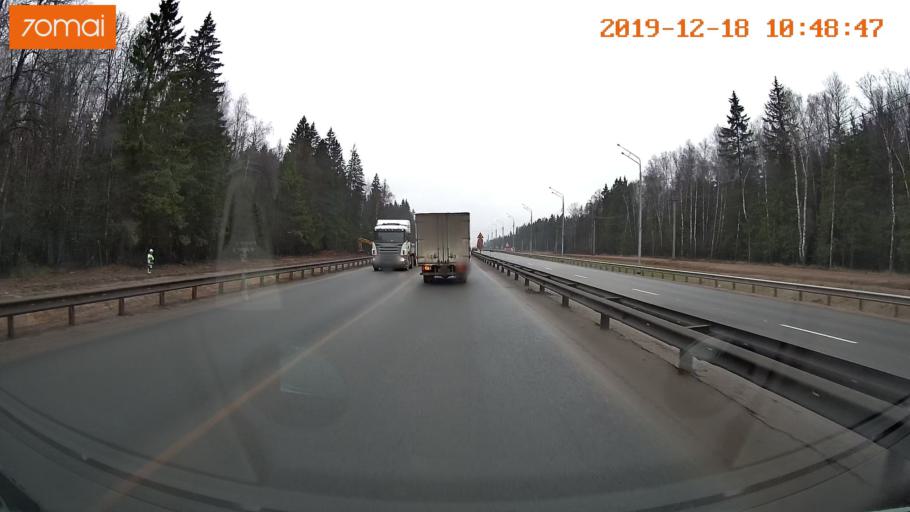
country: RU
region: Moskovskaya
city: Selyatino
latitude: 55.4993
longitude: 37.0233
